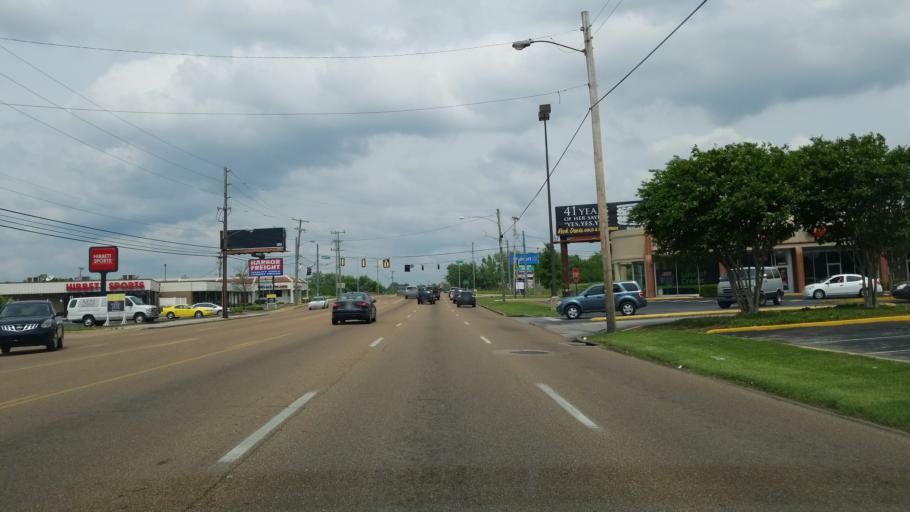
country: US
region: Tennessee
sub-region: Hamilton County
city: East Ridge
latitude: 35.0130
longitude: -85.2120
